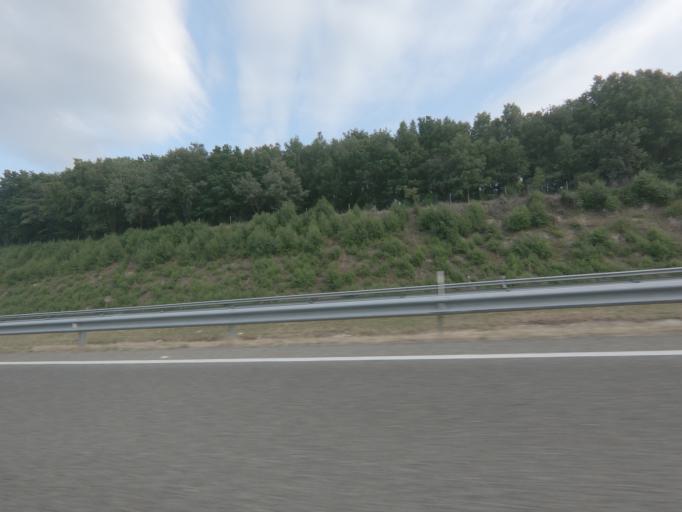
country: ES
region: Galicia
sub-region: Provincia de Ourense
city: Allariz
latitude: 42.2027
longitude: -7.7945
